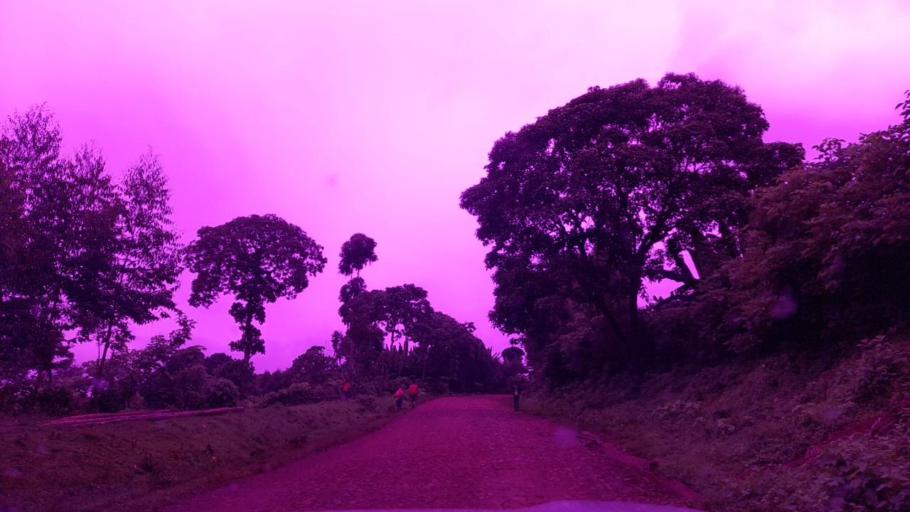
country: ET
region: Southern Nations, Nationalities, and People's Region
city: Tippi
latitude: 7.5813
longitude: 35.7733
